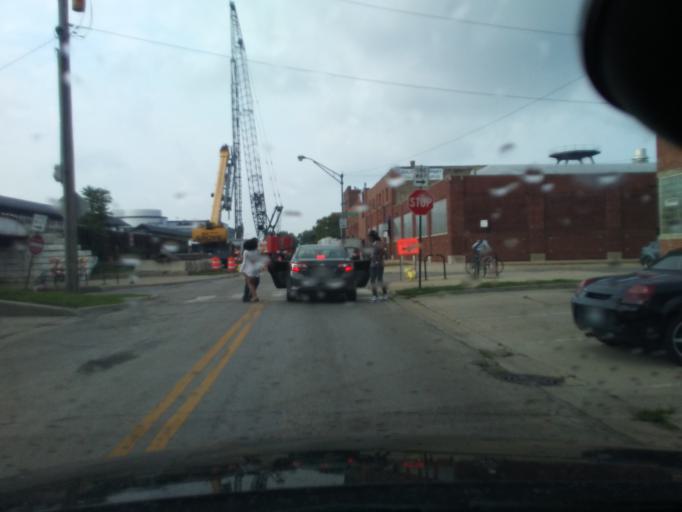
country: US
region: Illinois
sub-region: Cook County
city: Lincolnwood
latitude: 41.9667
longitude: -87.6741
